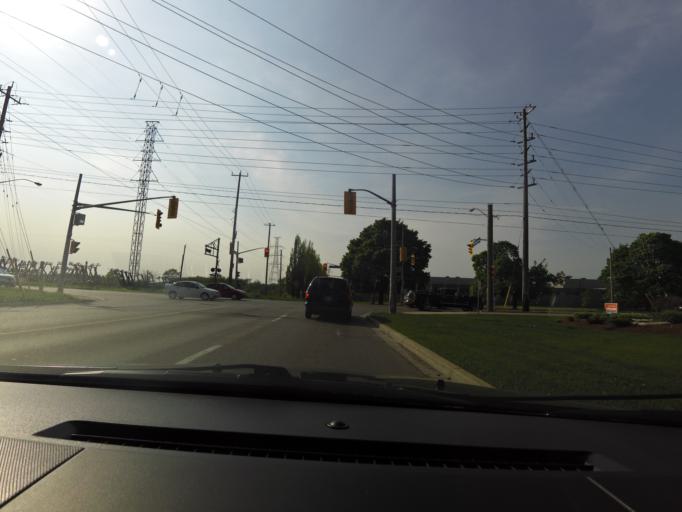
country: CA
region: Ontario
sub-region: Wellington County
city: Guelph
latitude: 43.5580
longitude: -80.2867
